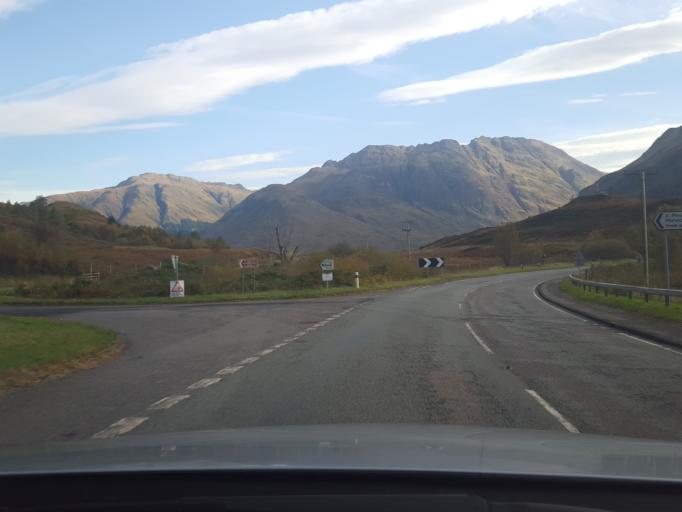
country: GB
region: Scotland
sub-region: Highland
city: Fort William
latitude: 57.2349
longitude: -5.4098
